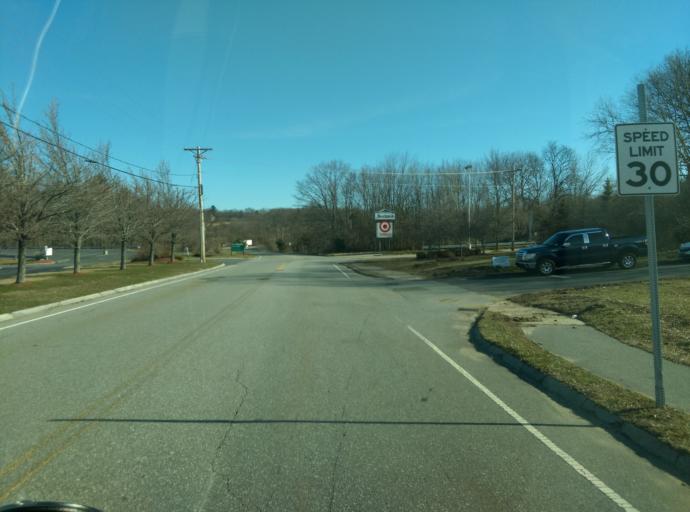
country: US
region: Massachusetts
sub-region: Essex County
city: Haverhill
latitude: 42.7859
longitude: -71.1193
